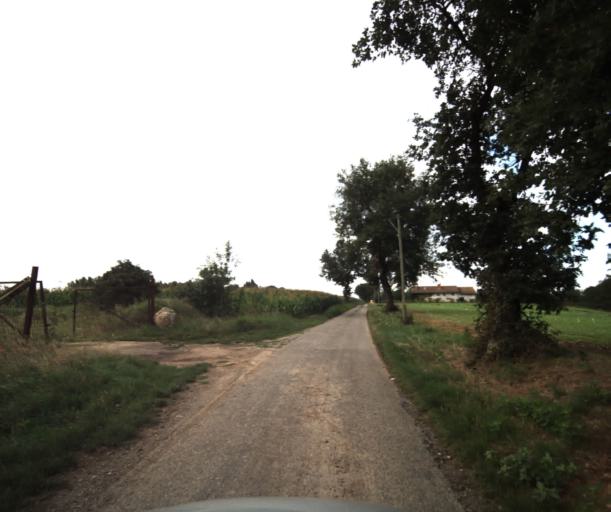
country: FR
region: Midi-Pyrenees
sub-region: Departement de la Haute-Garonne
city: Lacasse
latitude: 43.3889
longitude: 1.2378
